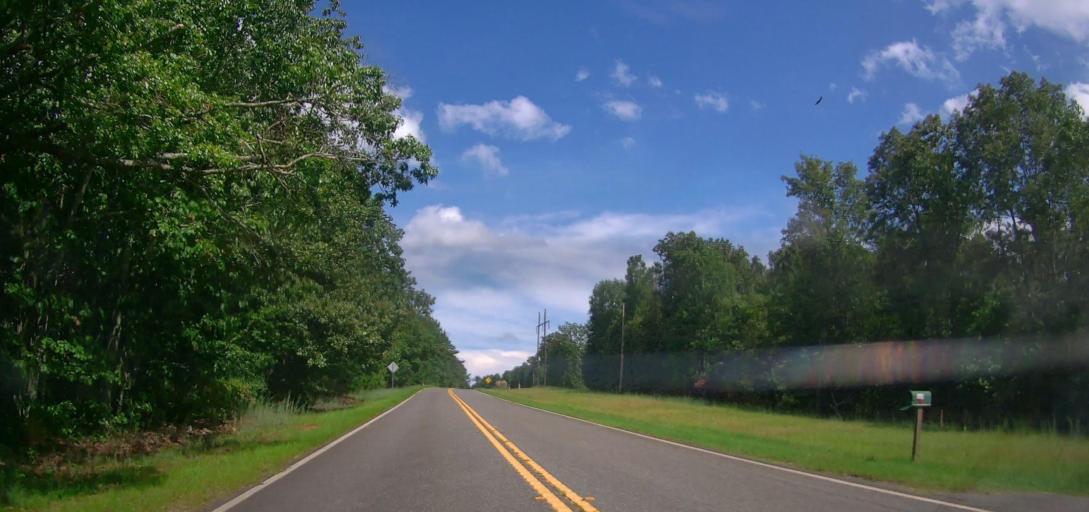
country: US
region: Georgia
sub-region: Meriwether County
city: Manchester
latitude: 32.8428
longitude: -84.6604
